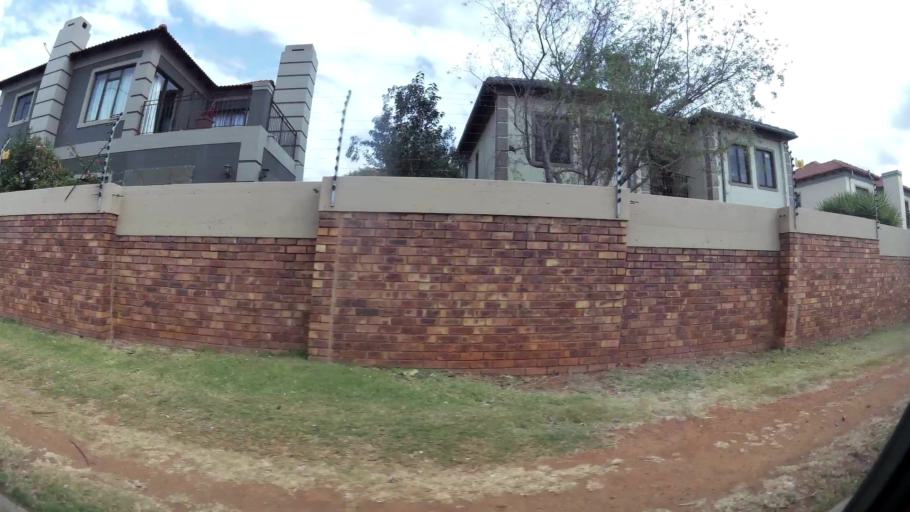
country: ZA
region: Gauteng
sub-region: City of Johannesburg Metropolitan Municipality
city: Roodepoort
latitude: -26.0954
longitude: 27.8771
